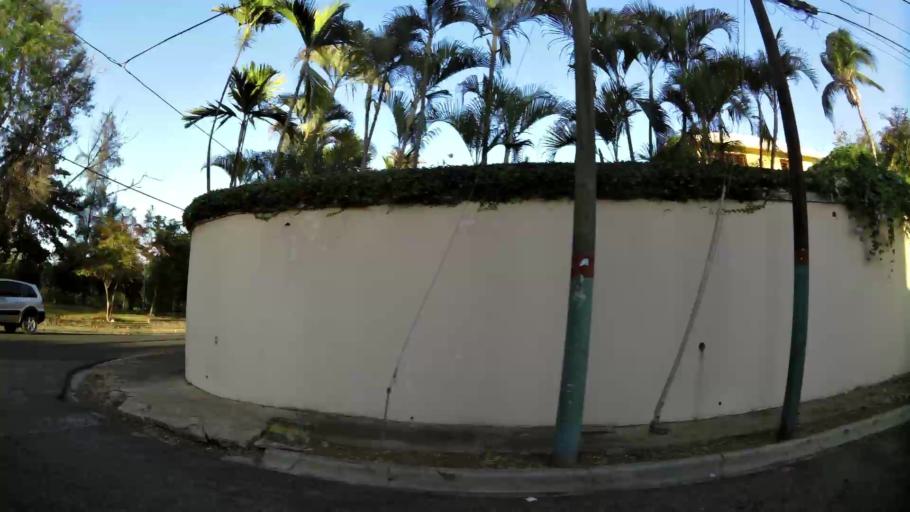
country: DO
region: Nacional
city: La Agustina
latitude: 18.4875
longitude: -69.9588
